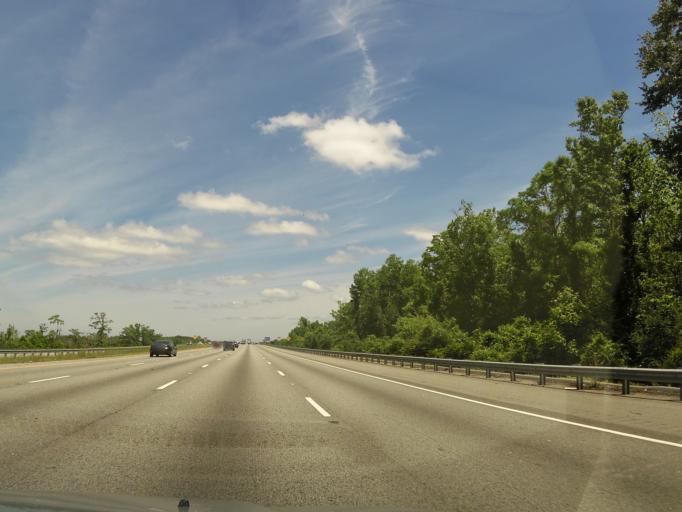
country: US
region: Georgia
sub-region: McIntosh County
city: Darien
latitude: 31.3687
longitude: -81.4561
